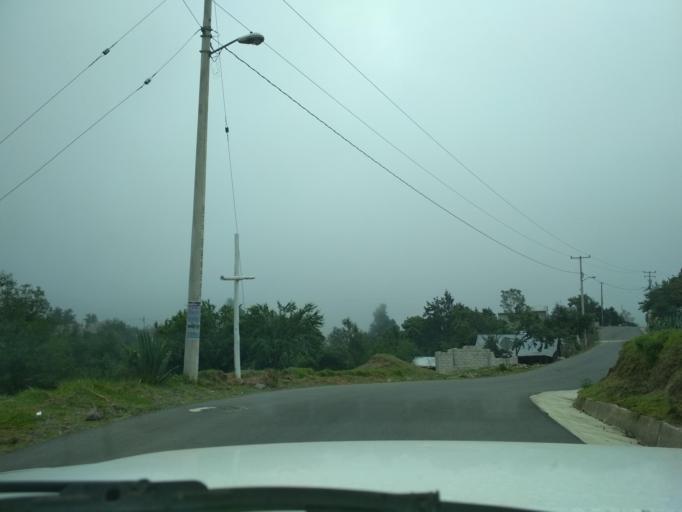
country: MX
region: Veracruz
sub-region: Mariano Escobedo
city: San Isidro el Berro
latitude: 18.9464
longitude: -97.2022
